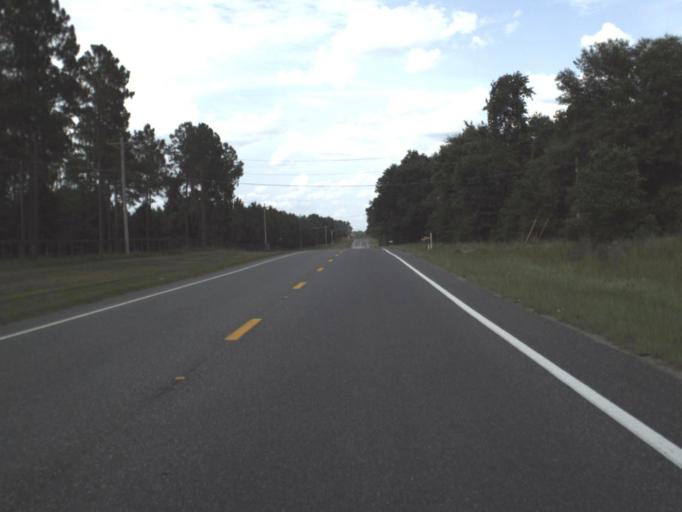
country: US
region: Florida
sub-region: Columbia County
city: Lake City
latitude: 30.0866
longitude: -82.6874
